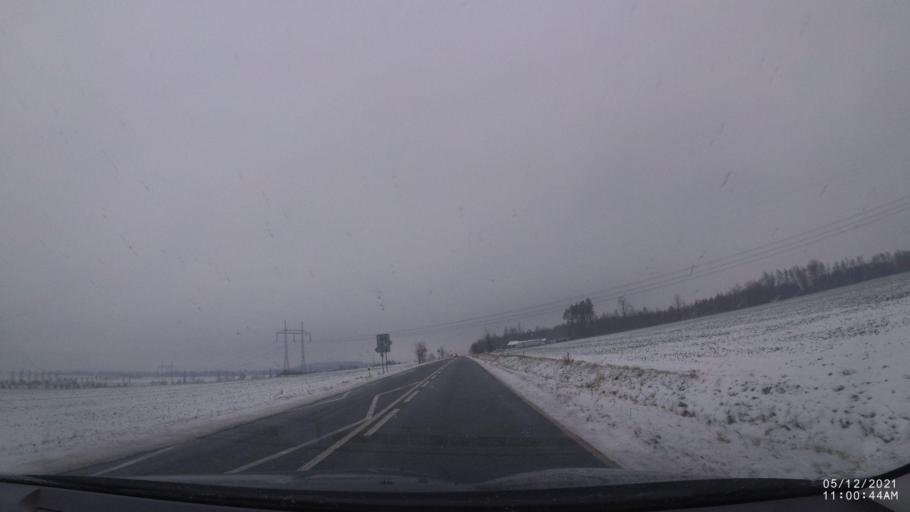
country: CZ
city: Solnice
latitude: 50.1675
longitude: 16.2198
